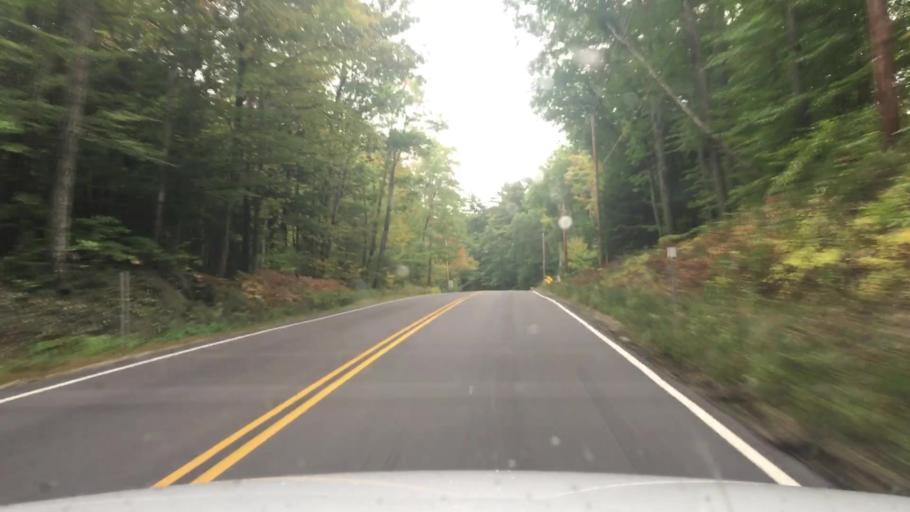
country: US
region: New Hampshire
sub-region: Carroll County
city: Wolfeboro
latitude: 43.5394
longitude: -71.2991
